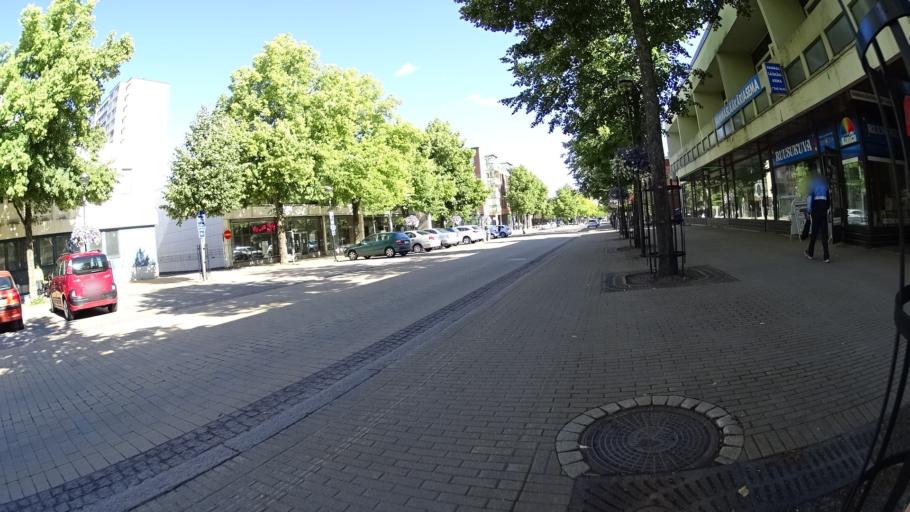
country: FI
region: Uusimaa
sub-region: Helsinki
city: Kerava
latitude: 60.4035
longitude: 25.1015
